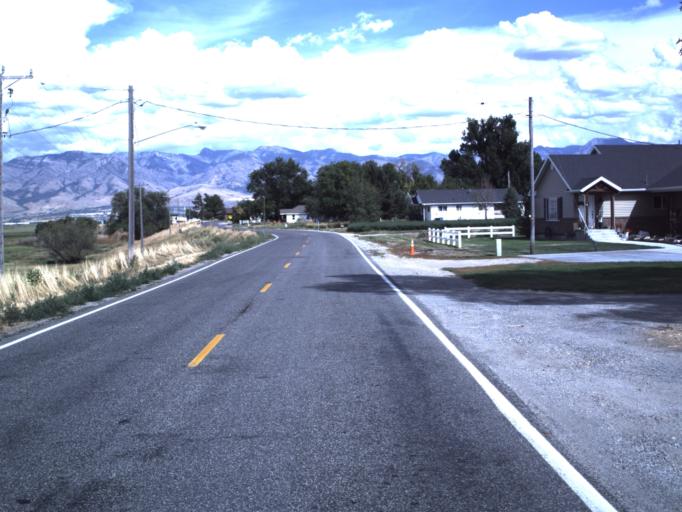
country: US
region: Utah
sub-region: Cache County
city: Lewiston
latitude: 41.9175
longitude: -111.9410
